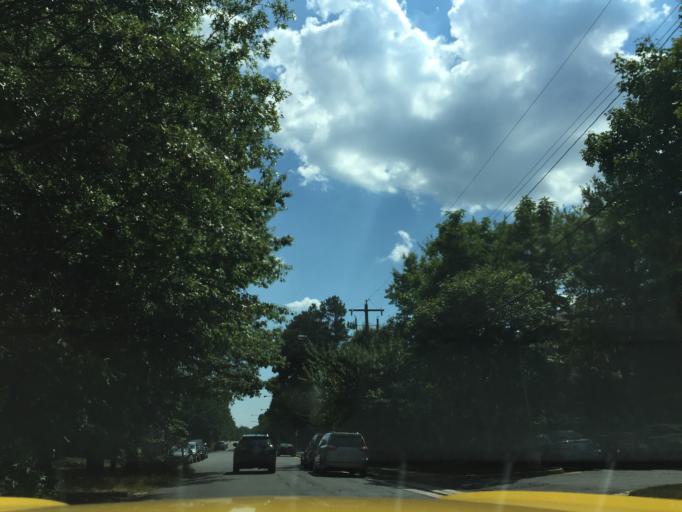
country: US
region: Virginia
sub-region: Fairfax County
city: Tysons Corner
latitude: 38.9106
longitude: -77.2261
